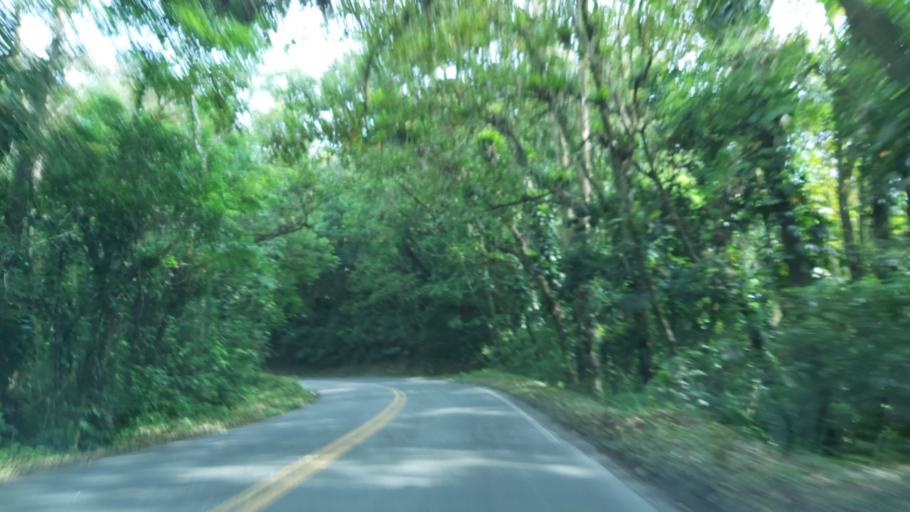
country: BR
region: Sao Paulo
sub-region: Juquia
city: Juquia
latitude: -24.1044
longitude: -47.6266
